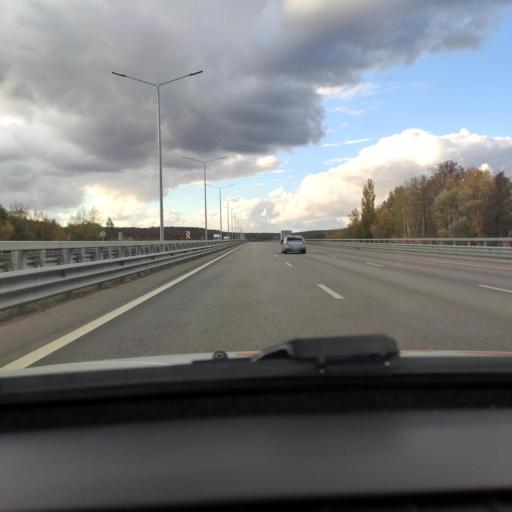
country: RU
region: Voronezj
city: Somovo
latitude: 51.7910
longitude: 39.2736
